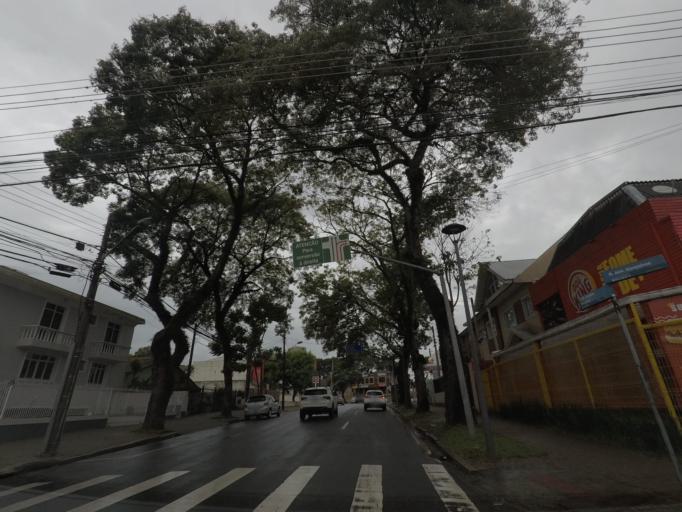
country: BR
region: Parana
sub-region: Curitiba
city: Curitiba
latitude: -25.4523
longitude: -49.2783
